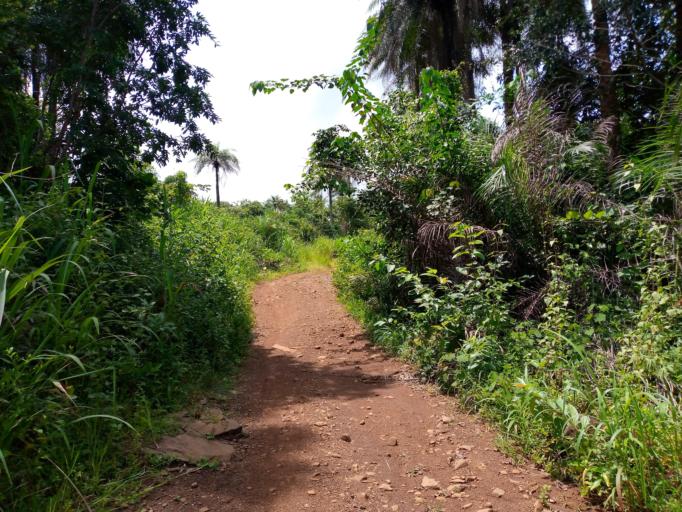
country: SL
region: Northern Province
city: Binkolo
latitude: 9.1186
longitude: -12.1338
